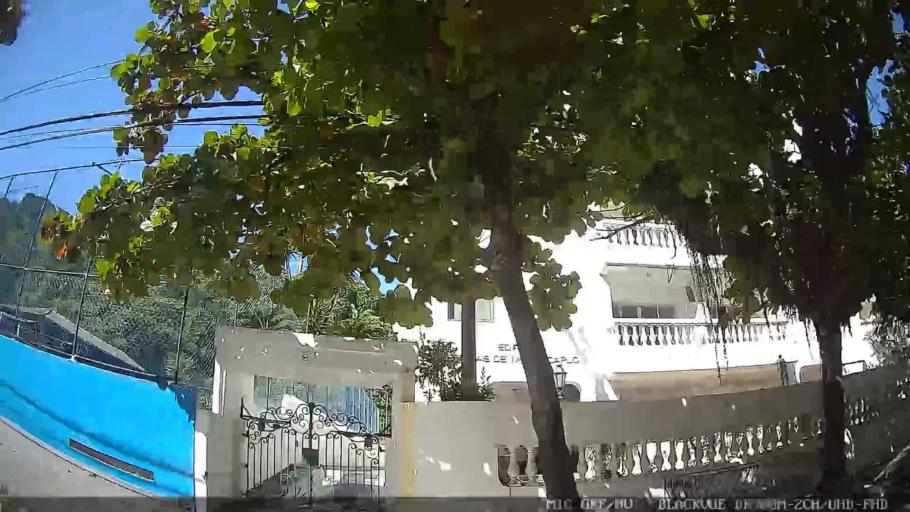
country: BR
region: Sao Paulo
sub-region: Guaruja
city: Guaruja
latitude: -23.9875
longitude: -46.2404
